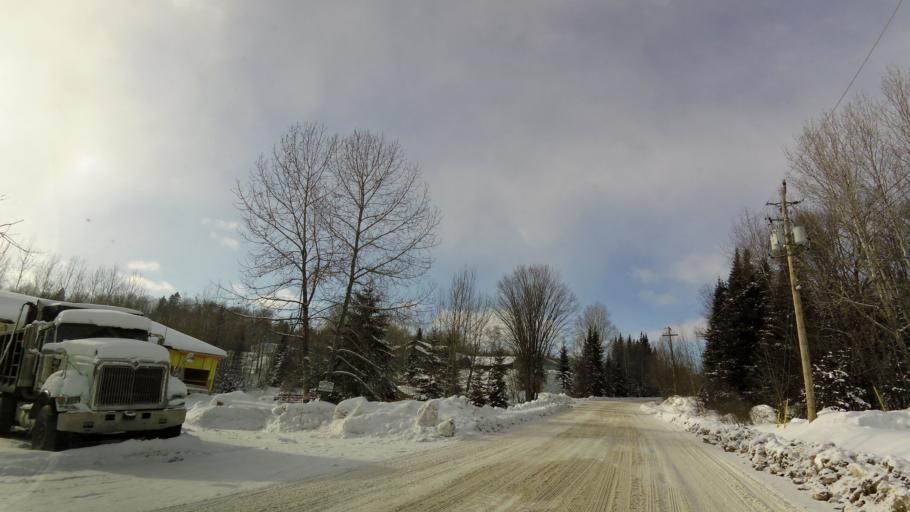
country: CA
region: Ontario
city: Bancroft
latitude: 45.0525
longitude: -78.5384
